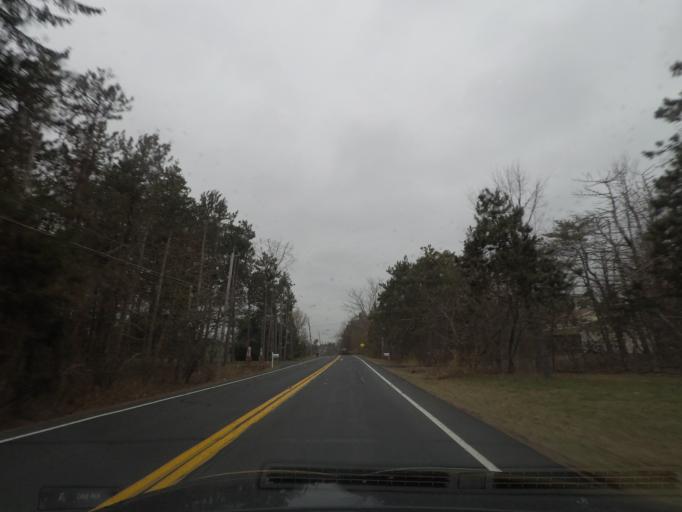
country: US
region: New York
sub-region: Rensselaer County
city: East Greenbush
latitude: 42.6136
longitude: -73.6715
